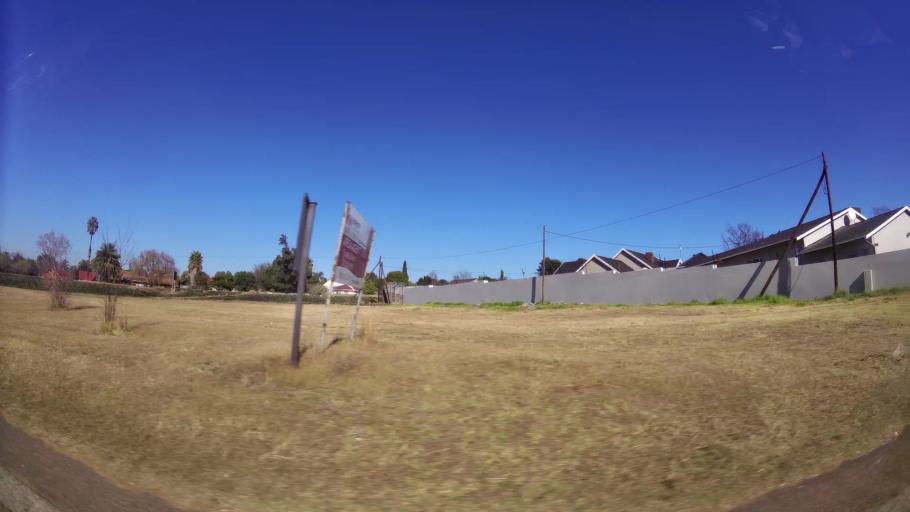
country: ZA
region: Mpumalanga
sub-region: Nkangala District Municipality
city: Witbank
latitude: -25.8907
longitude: 29.2370
